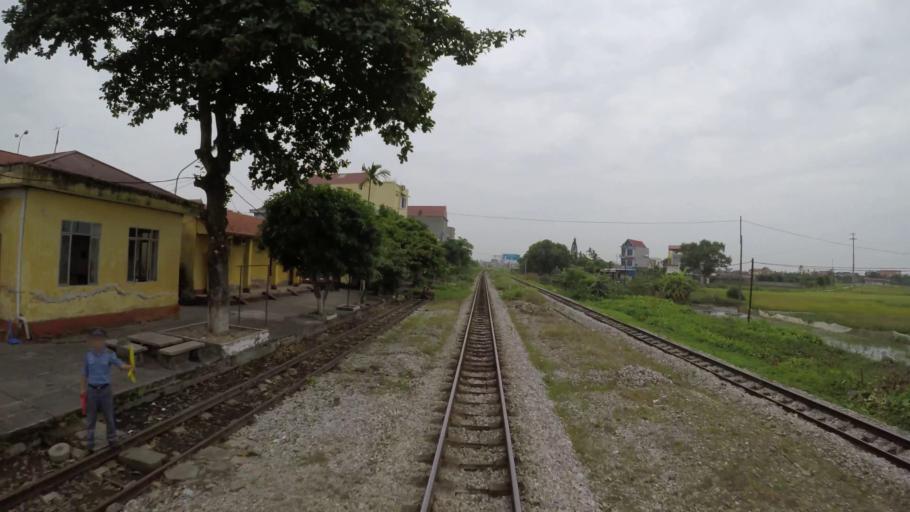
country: VN
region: Hai Duong
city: Phu Thai
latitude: 20.9328
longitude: 106.5522
